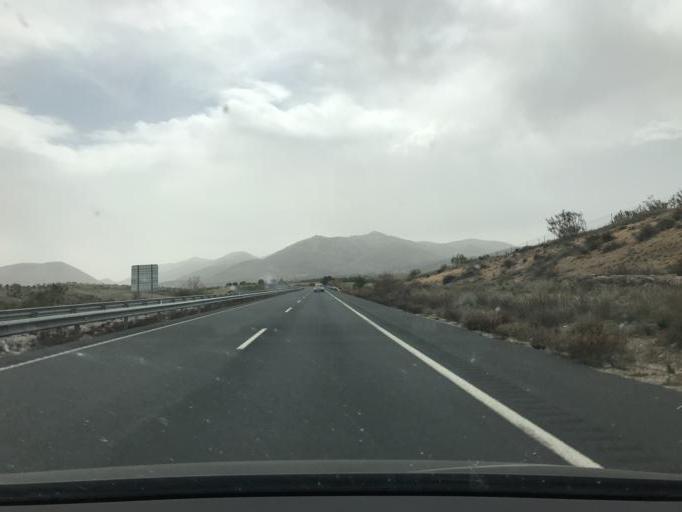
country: ES
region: Andalusia
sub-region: Provincia de Granada
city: Gor
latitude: 37.3961
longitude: -2.9784
